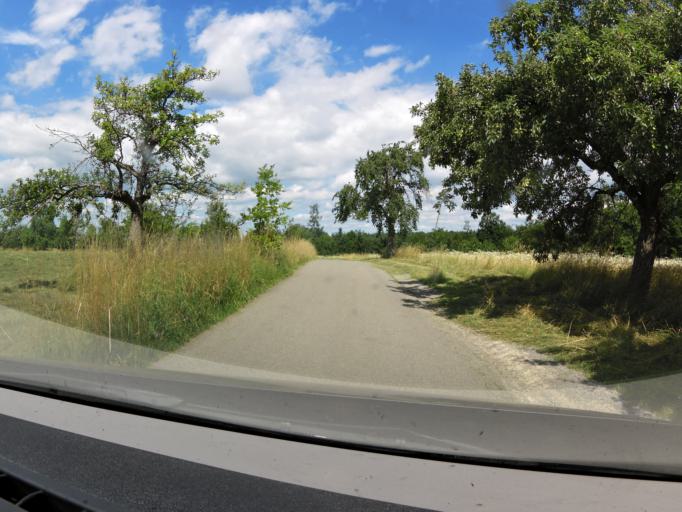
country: DE
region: Baden-Wuerttemberg
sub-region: Tuebingen Region
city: Tuebingen
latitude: 48.5529
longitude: 8.9944
